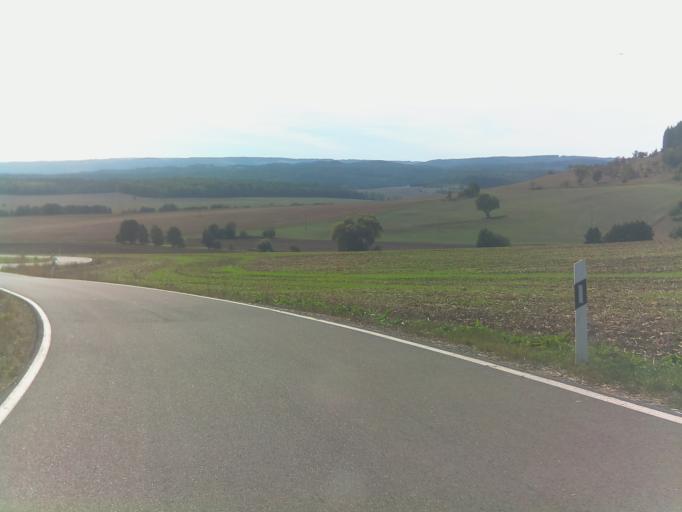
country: DE
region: Thuringia
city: Oberkatz
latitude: 50.5728
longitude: 10.2412
